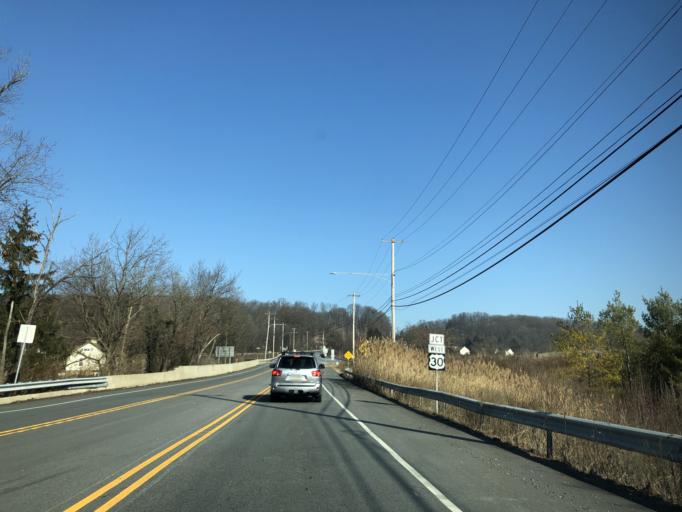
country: US
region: Pennsylvania
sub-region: Chester County
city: Downingtown
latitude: 40.0177
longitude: -75.6948
